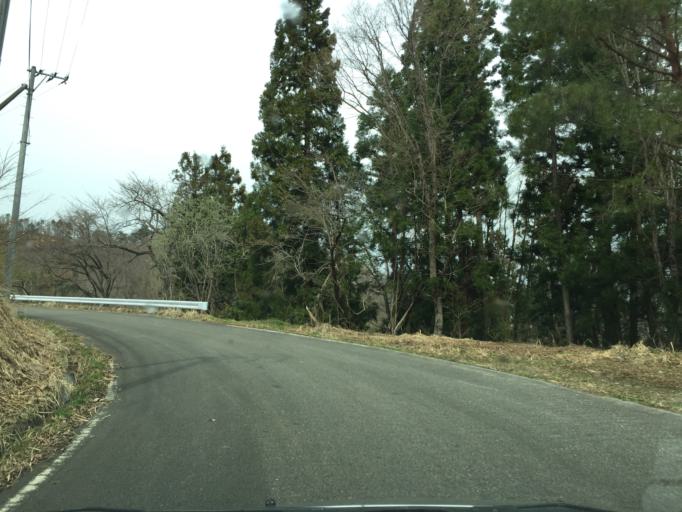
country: JP
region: Fukushima
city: Kitakata
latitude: 37.4769
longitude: 139.8097
